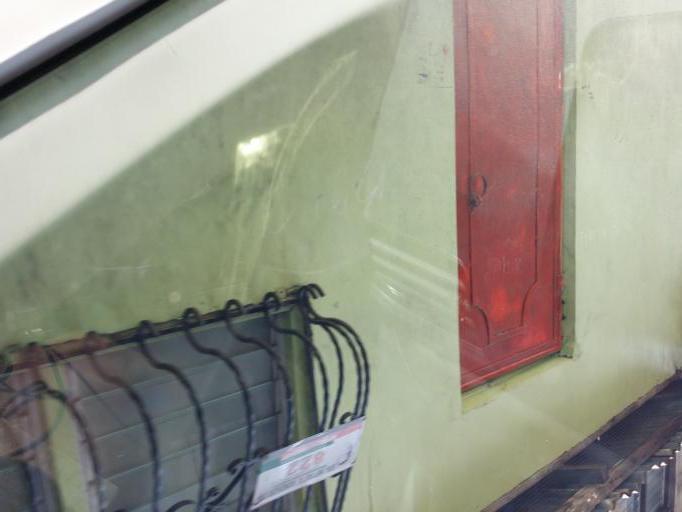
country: PH
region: Metro Manila
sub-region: Mandaluyong
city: Mandaluyong City
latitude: 14.5747
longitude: 121.0288
